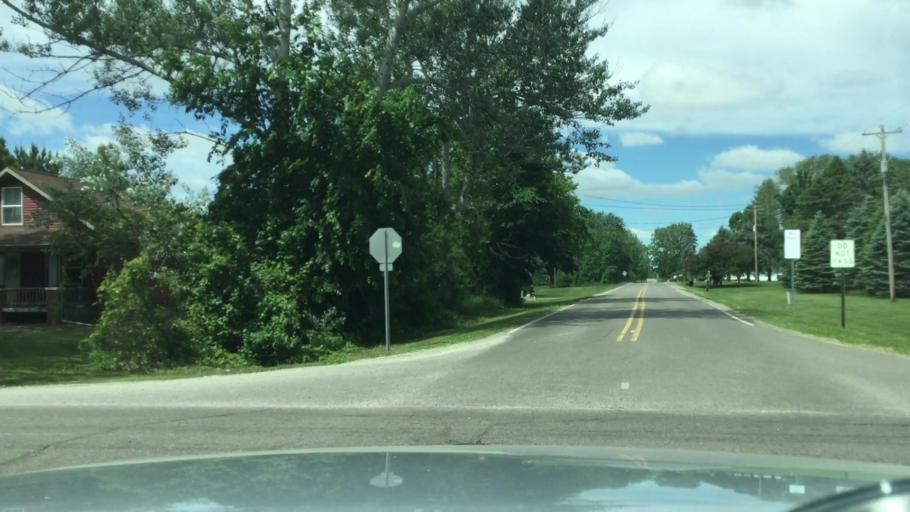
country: US
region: Michigan
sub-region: Genesee County
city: Clio
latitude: 43.1919
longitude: -83.7743
